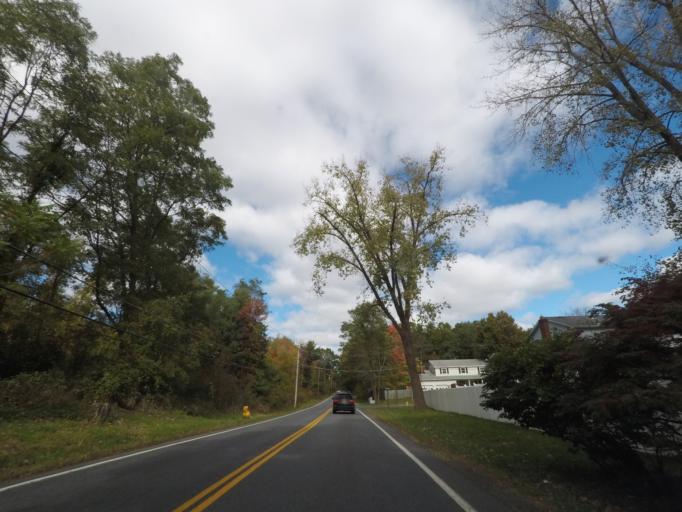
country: US
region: New York
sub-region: Saratoga County
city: Country Knolls
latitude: 42.8443
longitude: -73.7698
